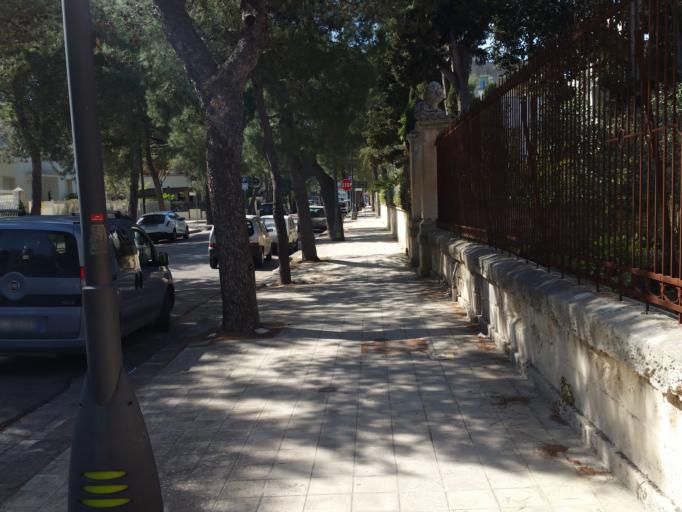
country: IT
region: Apulia
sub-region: Provincia di Lecce
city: Lecce
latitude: 40.3481
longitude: 18.1837
